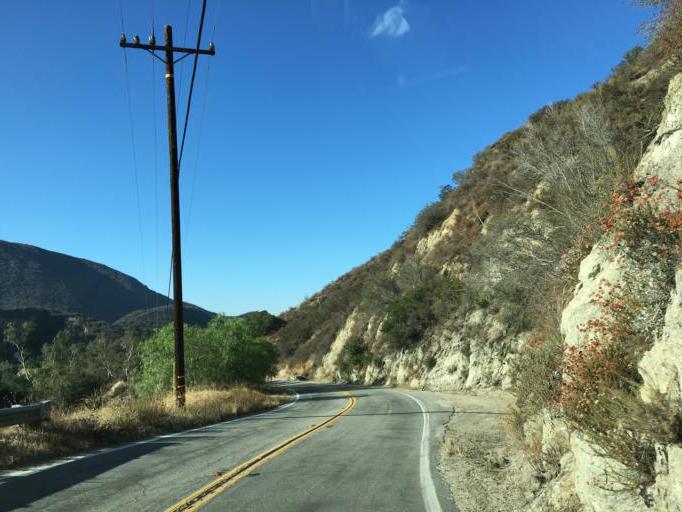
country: US
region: California
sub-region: Los Angeles County
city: San Fernando
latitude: 34.3255
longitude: -118.3385
